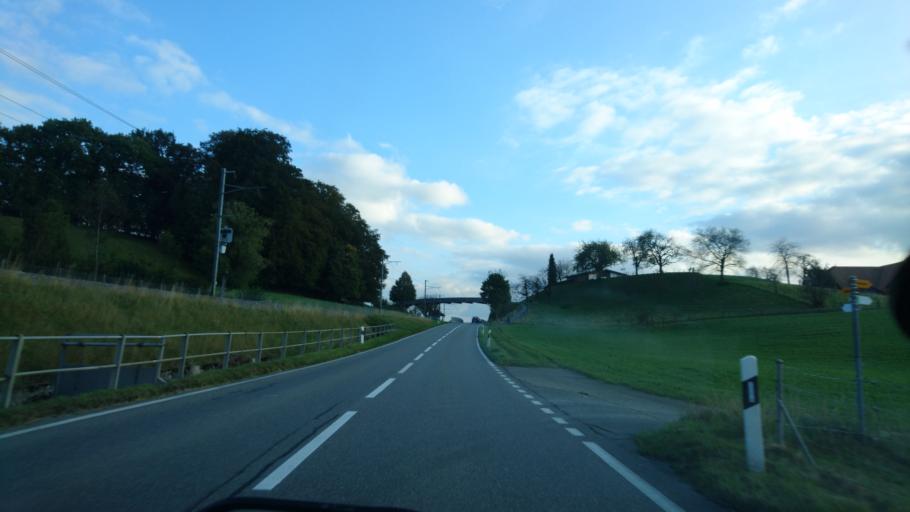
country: CH
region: Bern
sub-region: Bern-Mittelland District
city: Vechigen
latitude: 46.9483
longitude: 7.5557
